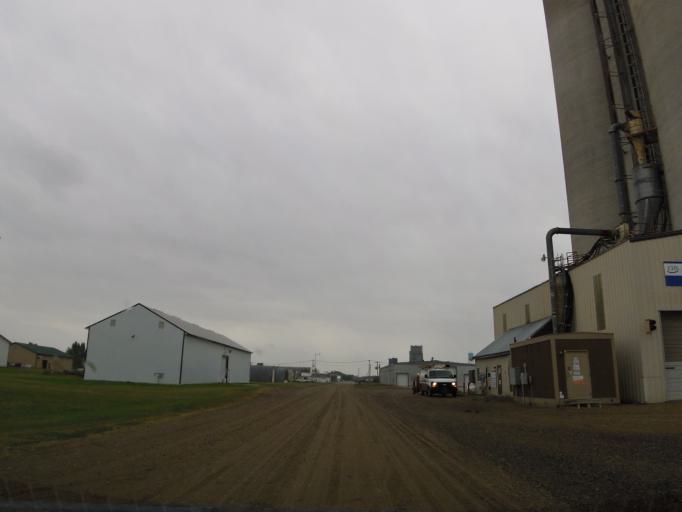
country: US
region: Minnesota
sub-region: Marshall County
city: Warren
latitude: 48.4557
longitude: -96.8747
